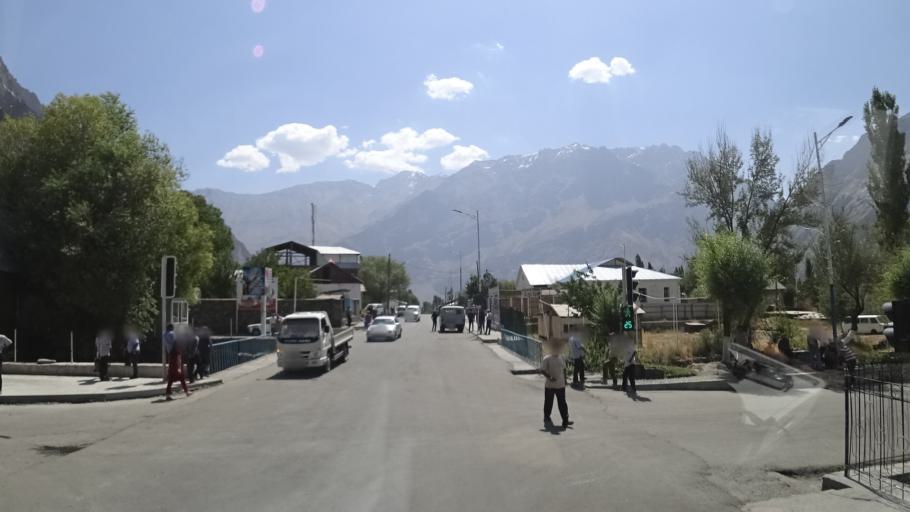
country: TJ
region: Gorno-Badakhshan
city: Rushon
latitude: 37.9472
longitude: 71.5585
